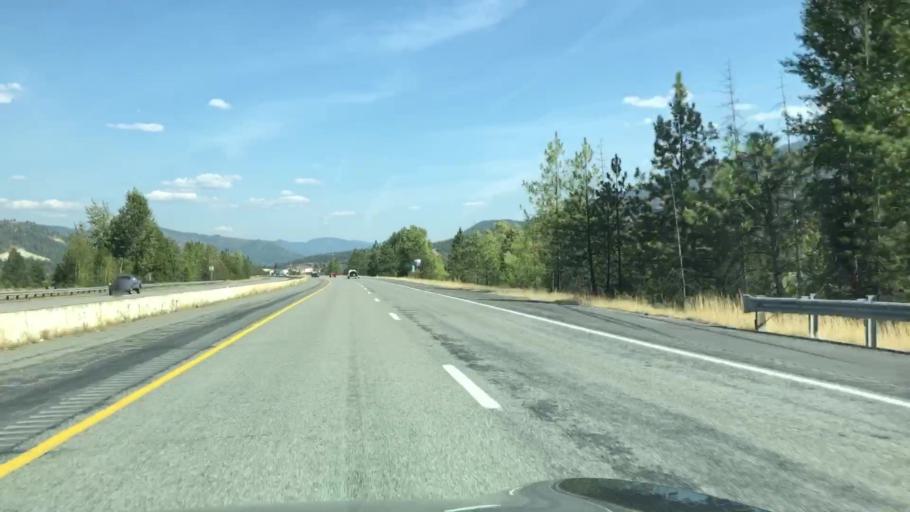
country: US
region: Idaho
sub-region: Shoshone County
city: Pinehurst
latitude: 47.5467
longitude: -116.2128
